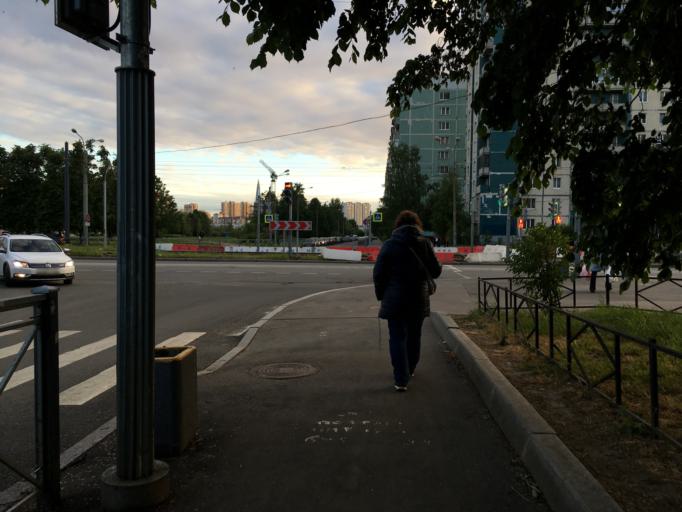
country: RU
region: St.-Petersburg
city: Staraya Derevnya
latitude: 60.0156
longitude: 30.2409
